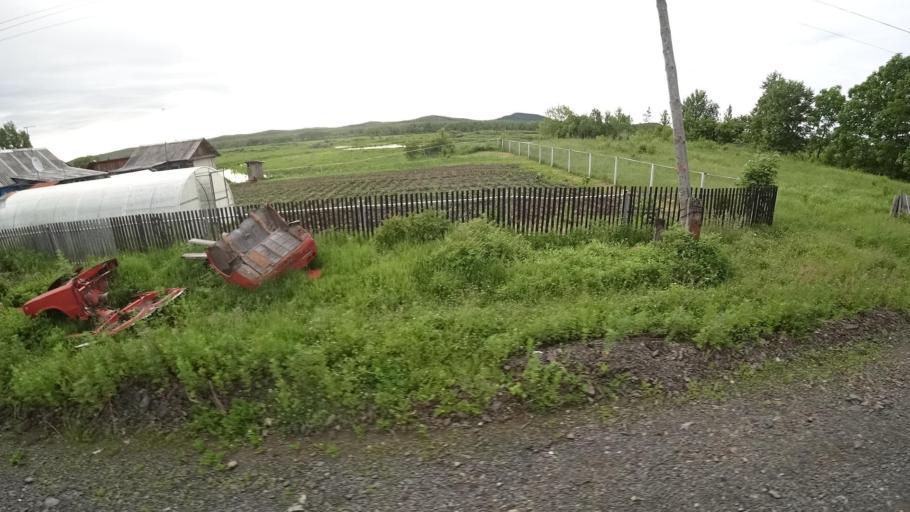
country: RU
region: Khabarovsk Krai
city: Amursk
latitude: 49.8896
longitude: 136.1296
